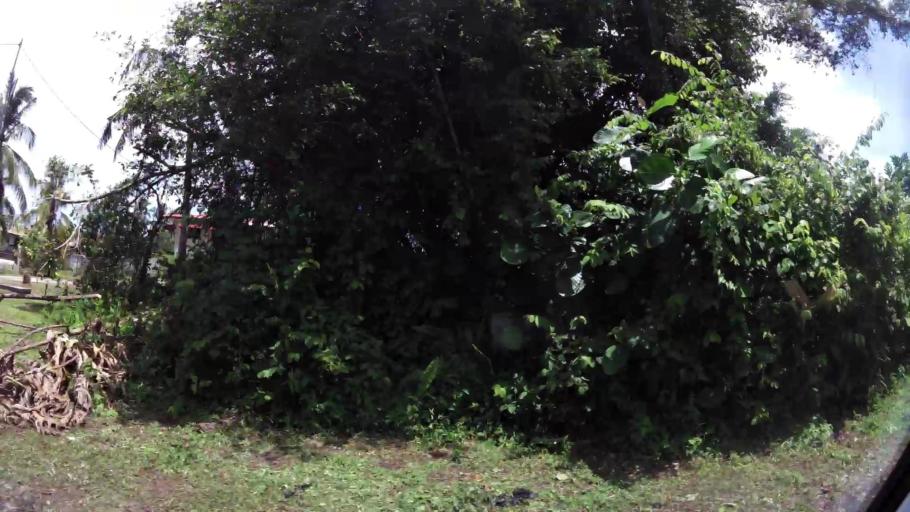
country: BN
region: Belait
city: Kuala Belait
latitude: 4.5812
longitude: 114.2472
